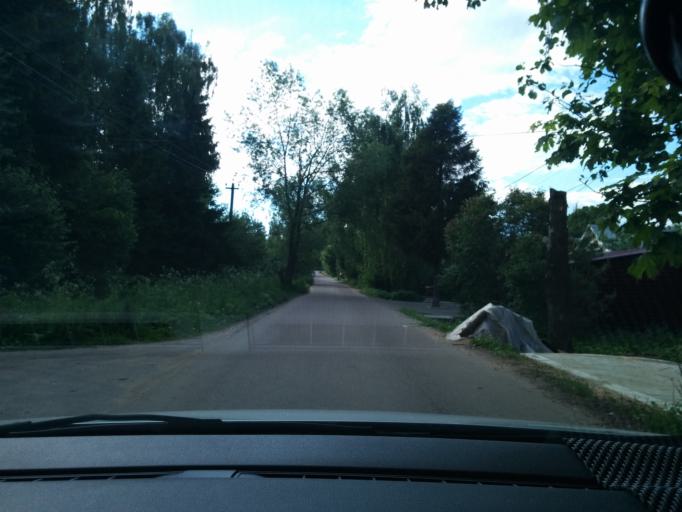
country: RU
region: Moskovskaya
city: Lugovaya
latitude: 56.0530
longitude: 37.4808
